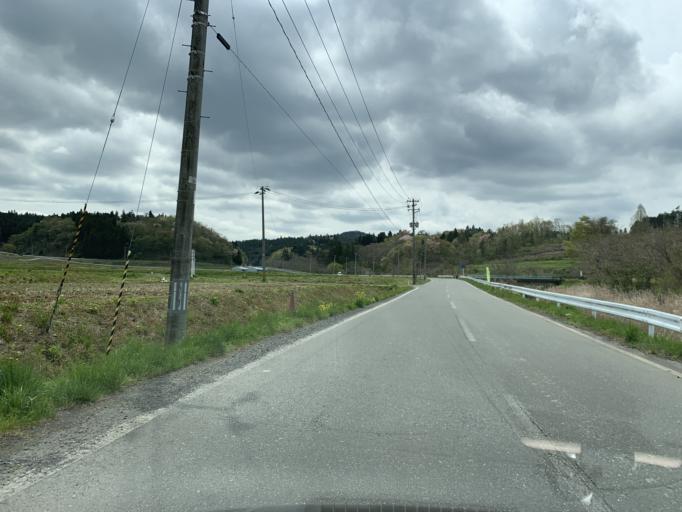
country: JP
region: Iwate
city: Ichinoseki
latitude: 38.8487
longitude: 141.3398
